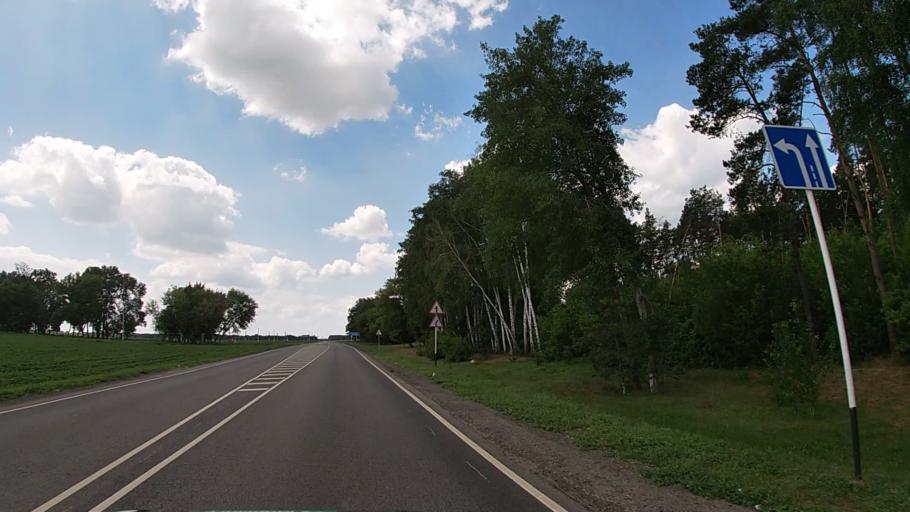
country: RU
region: Belgorod
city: Golovchino
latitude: 50.5061
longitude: 35.7430
